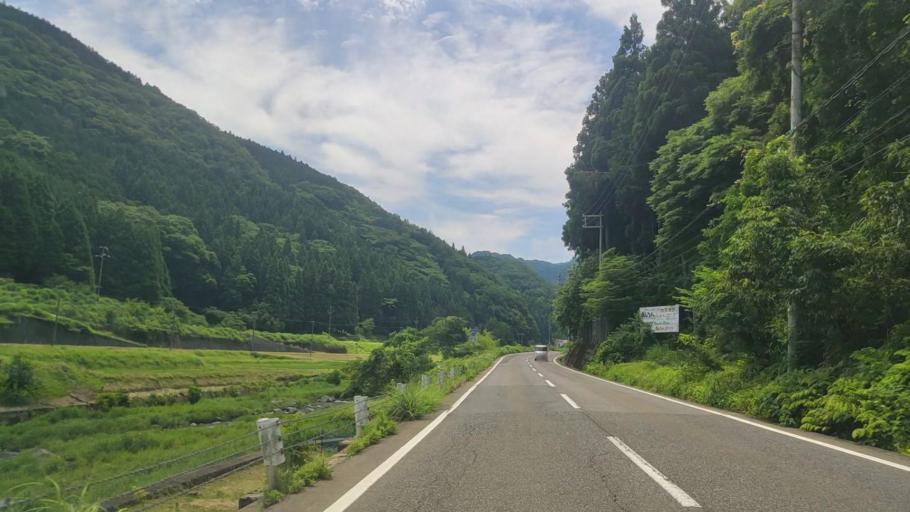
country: JP
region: Hyogo
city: Toyooka
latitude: 35.4790
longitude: 134.5519
